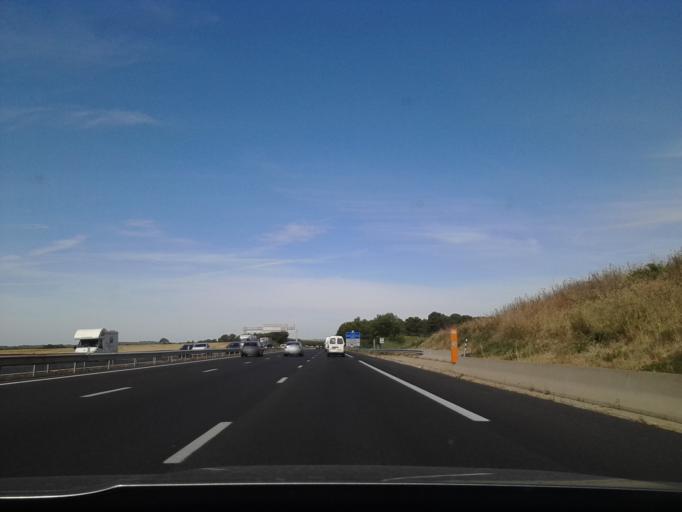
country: FR
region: Languedoc-Roussillon
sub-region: Departement de l'Herault
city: Montblanc
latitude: 43.3625
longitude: 3.3662
